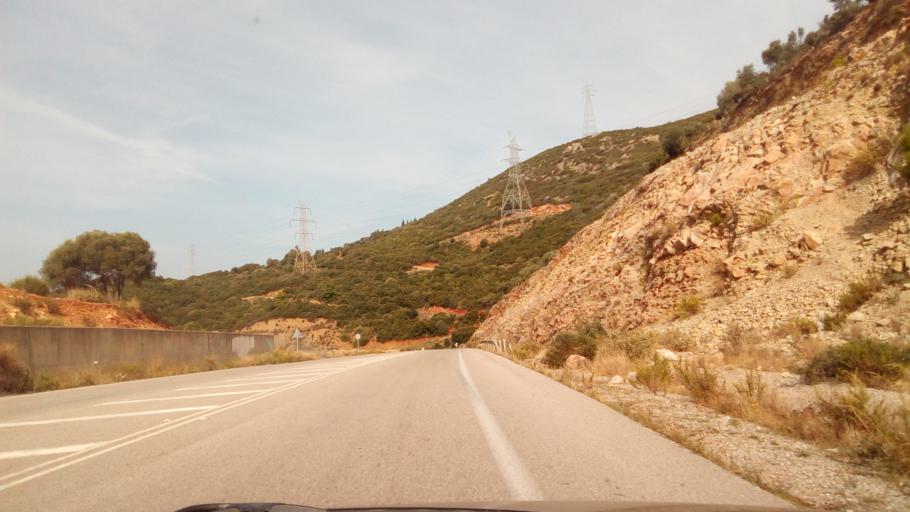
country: GR
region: West Greece
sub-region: Nomos Aitolias kai Akarnanias
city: Nafpaktos
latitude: 38.3996
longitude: 21.8223
